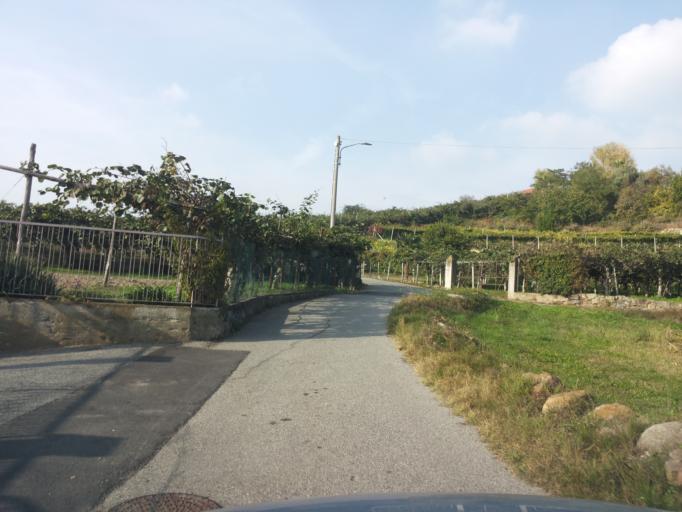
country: IT
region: Piedmont
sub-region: Provincia di Biella
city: Viverone
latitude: 45.4291
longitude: 8.0523
